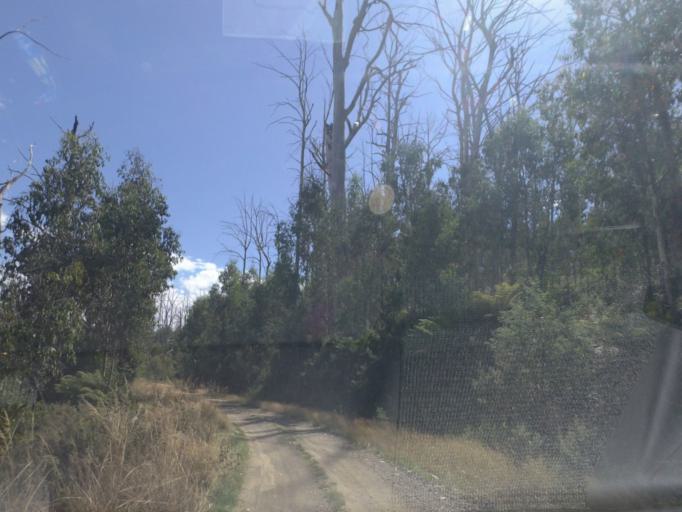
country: AU
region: Victoria
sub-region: Murrindindi
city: Alexandra
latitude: -37.4638
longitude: 145.8235
